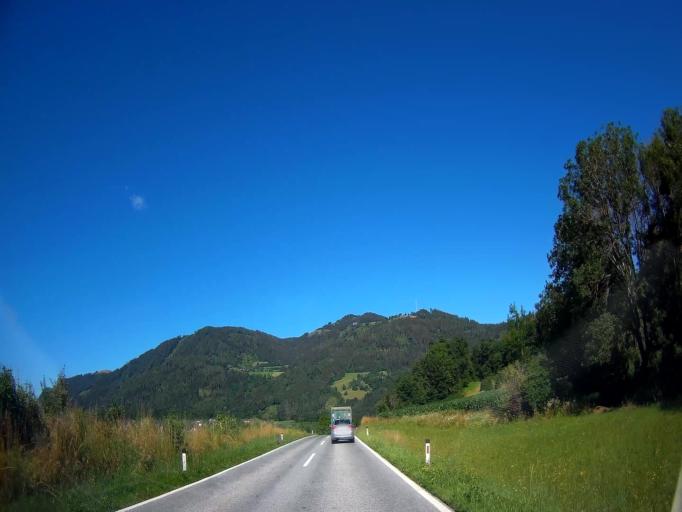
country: AT
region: Carinthia
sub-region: Politischer Bezirk Sankt Veit an der Glan
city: Bruckl
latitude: 46.7248
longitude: 14.5378
